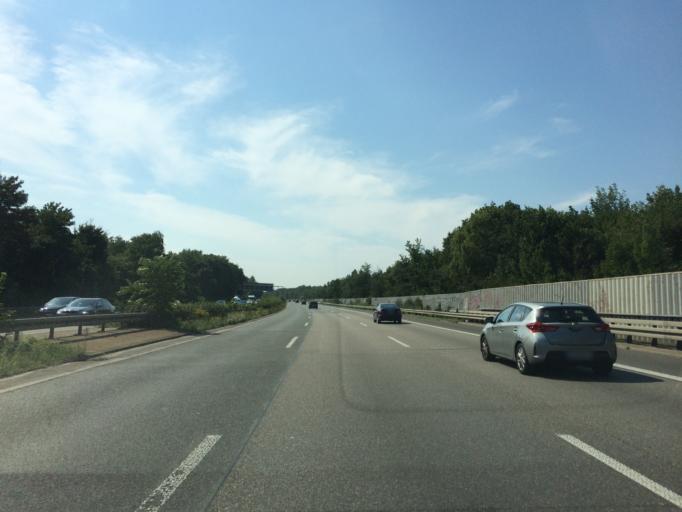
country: DE
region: North Rhine-Westphalia
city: Castrop-Rauxel
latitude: 51.6042
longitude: 7.3118
